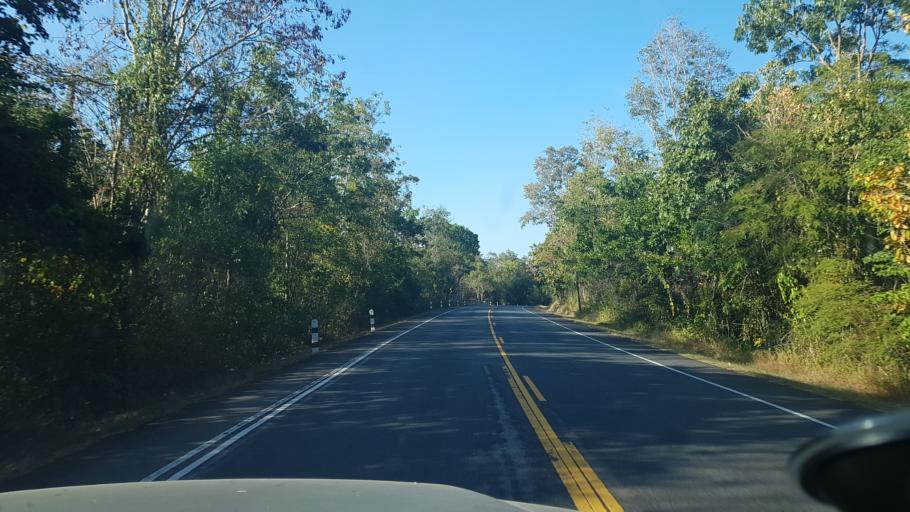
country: TH
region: Phetchabun
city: Nam Nao
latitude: 16.7550
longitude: 101.4625
